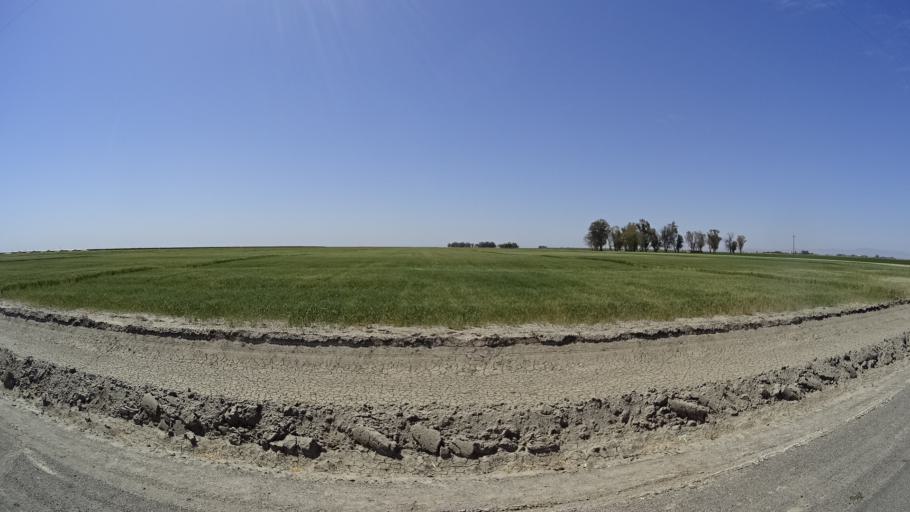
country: US
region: California
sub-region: Kings County
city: Stratford
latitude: 36.1900
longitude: -119.7602
